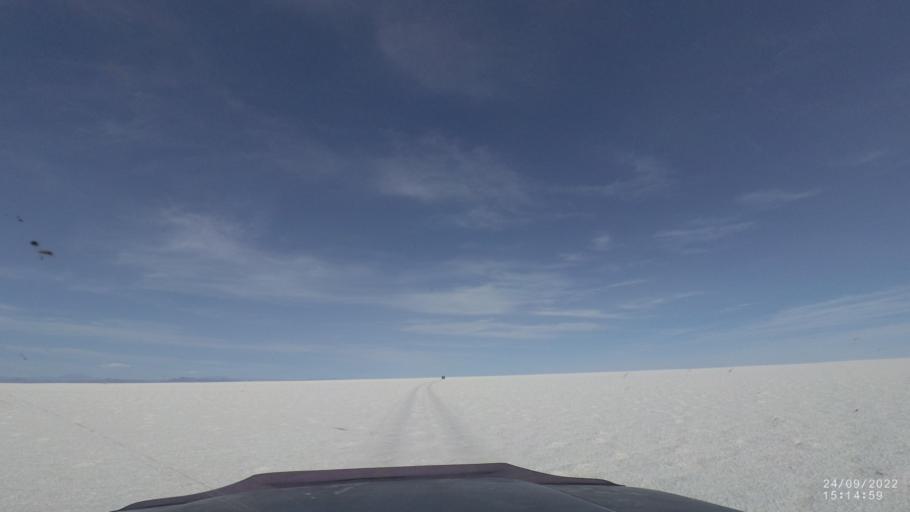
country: BO
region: Potosi
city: Colchani
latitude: -19.9689
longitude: -67.4498
